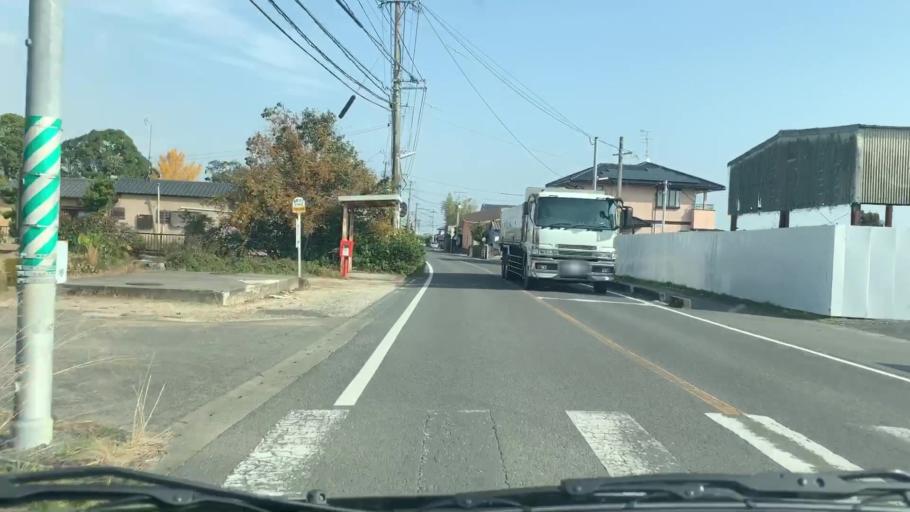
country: JP
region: Saga Prefecture
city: Saga-shi
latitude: 33.3035
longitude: 130.2431
